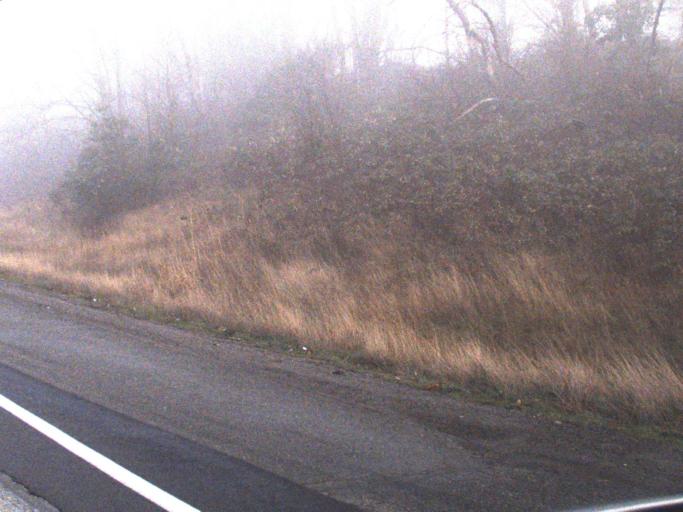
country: US
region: Washington
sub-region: King County
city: Des Moines
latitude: 47.3862
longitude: -122.2900
